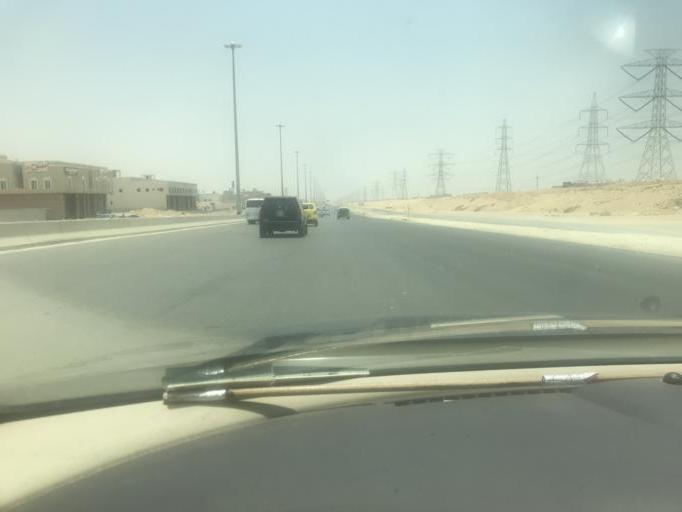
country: SA
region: Ar Riyad
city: Riyadh
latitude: 24.8177
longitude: 46.7344
